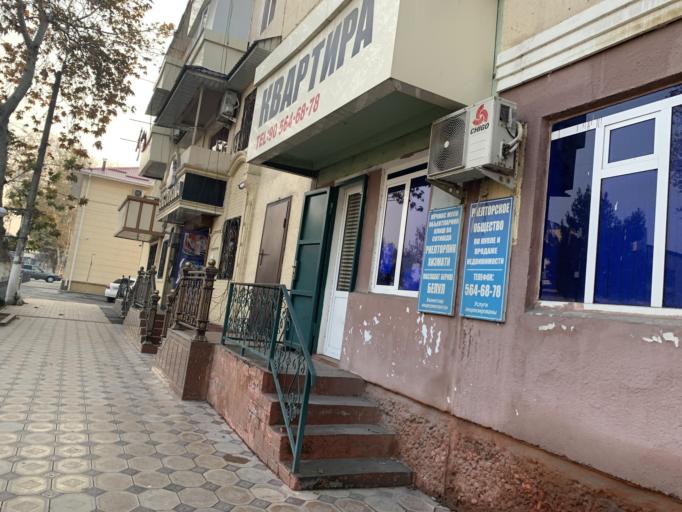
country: UZ
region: Fergana
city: Qo`qon
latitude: 40.5278
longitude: 70.9392
